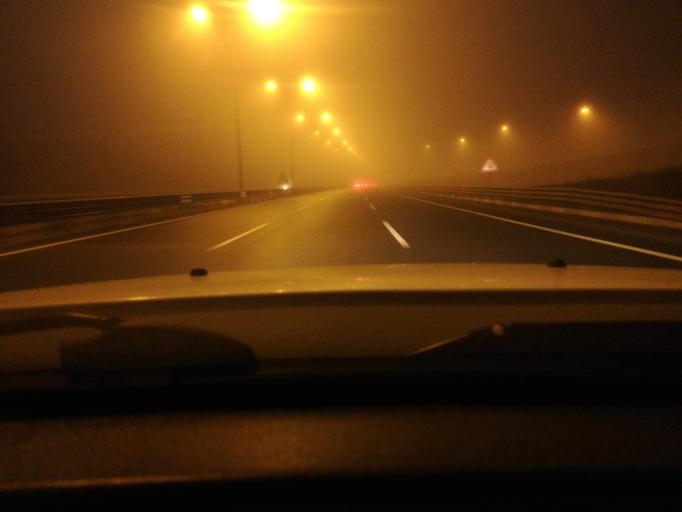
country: TR
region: Istanbul
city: Sultanbeyli
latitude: 40.9629
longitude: 29.3206
